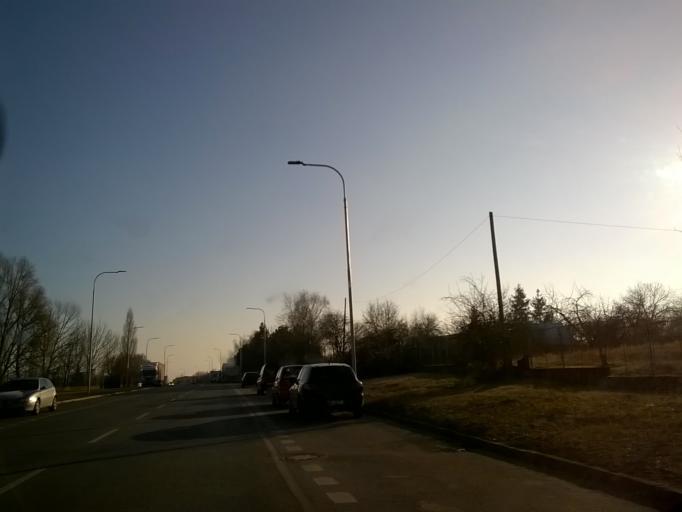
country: SK
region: Nitriansky
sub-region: Okres Nitra
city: Nitra
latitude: 48.3012
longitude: 18.0515
